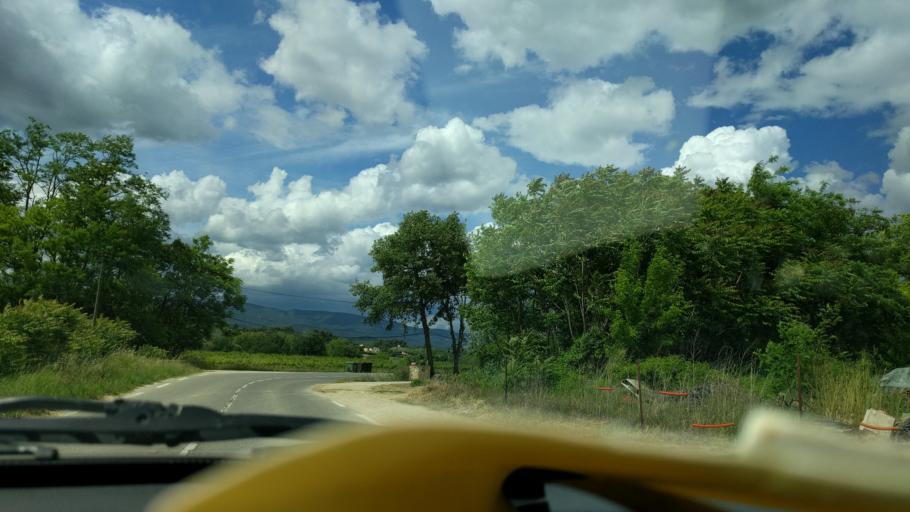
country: FR
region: Provence-Alpes-Cote d'Azur
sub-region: Departement du Vaucluse
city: Grambois
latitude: 43.7248
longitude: 5.5545
